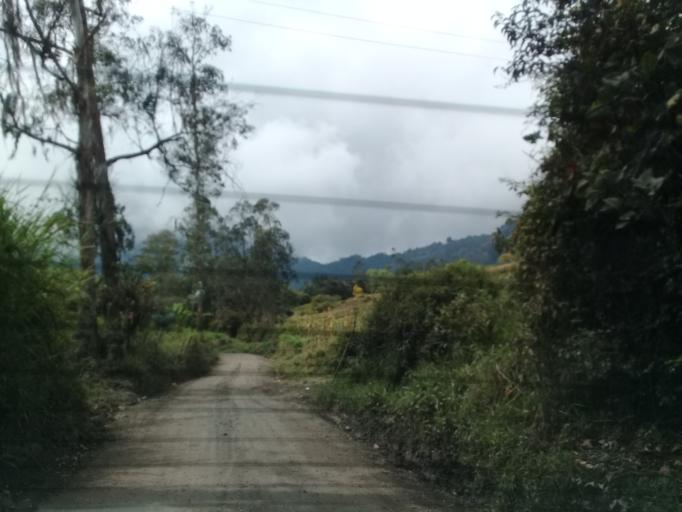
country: CO
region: Cundinamarca
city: Caqueza
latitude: 4.4119
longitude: -73.9862
